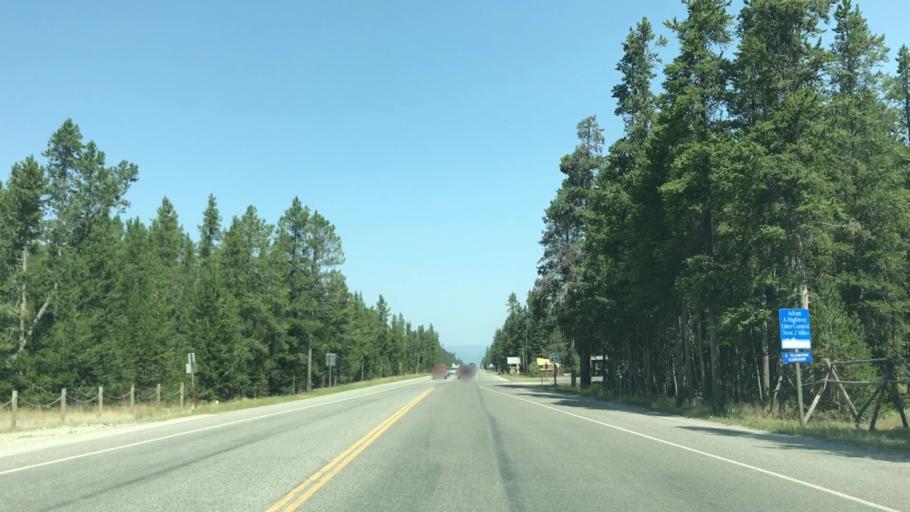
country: US
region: Montana
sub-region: Gallatin County
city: West Yellowstone
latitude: 44.6658
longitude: -111.0998
